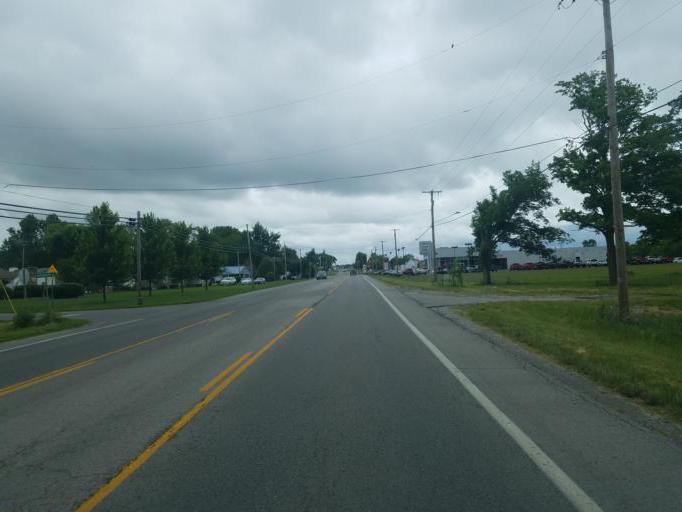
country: US
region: Ohio
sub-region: Marion County
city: Marion
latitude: 40.5516
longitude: -83.1148
